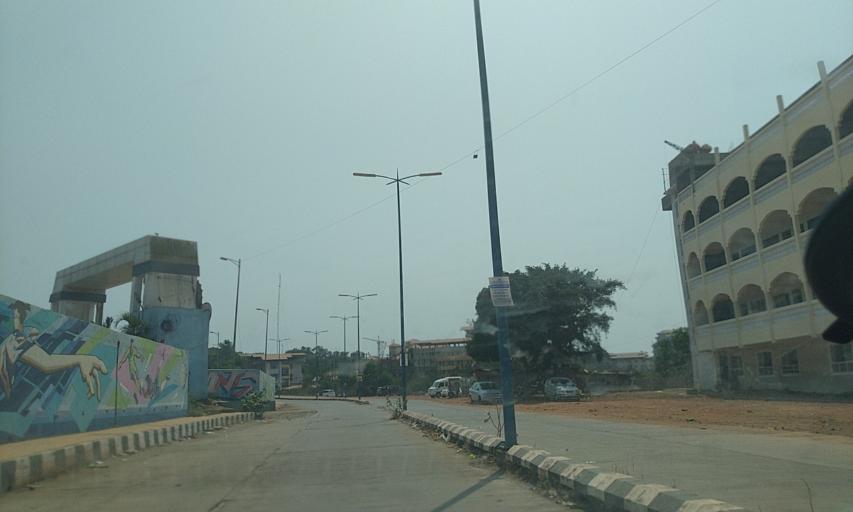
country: IN
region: Goa
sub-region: North Goa
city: Bambolim
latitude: 15.4677
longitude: 73.8609
